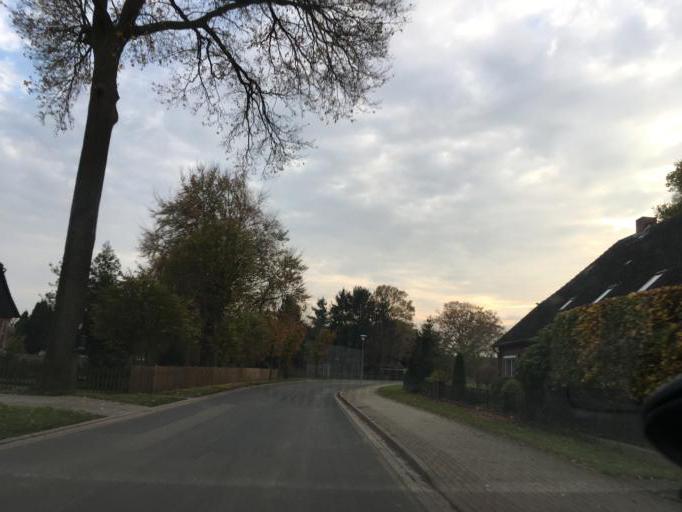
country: DE
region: Lower Saxony
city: Bergen
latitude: 52.8453
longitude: 9.9729
